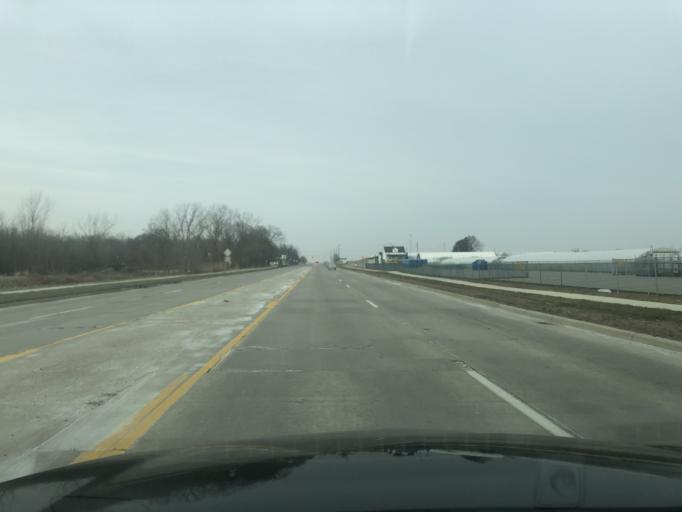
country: US
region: Michigan
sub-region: Wayne County
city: Taylor
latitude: 42.1957
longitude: -83.3212
